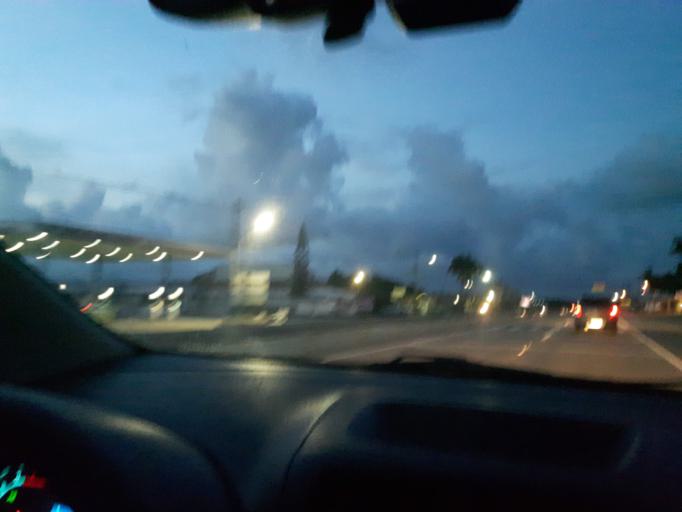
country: BR
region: Alagoas
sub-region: Marechal Deodoro
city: Marechal Deodoro
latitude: -9.7740
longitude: -35.8523
